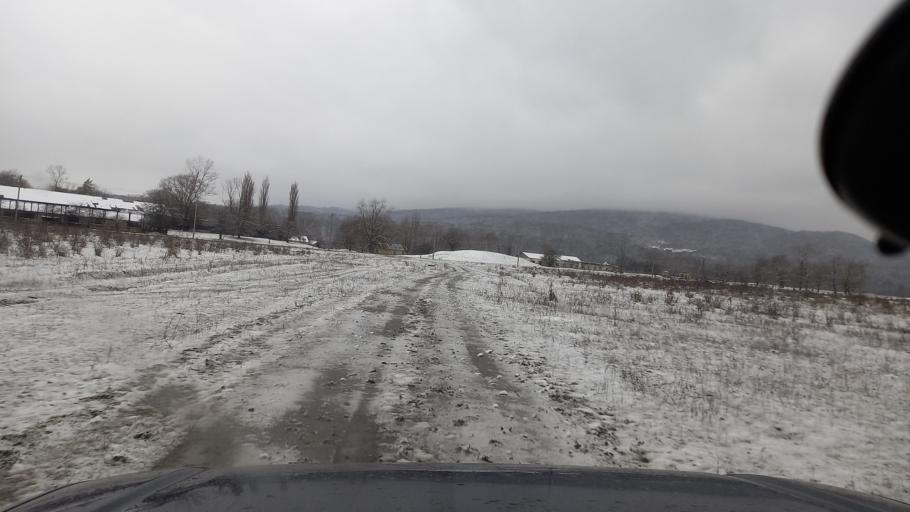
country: RU
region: Adygeya
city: Kamennomostskiy
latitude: 44.2240
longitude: 40.1816
